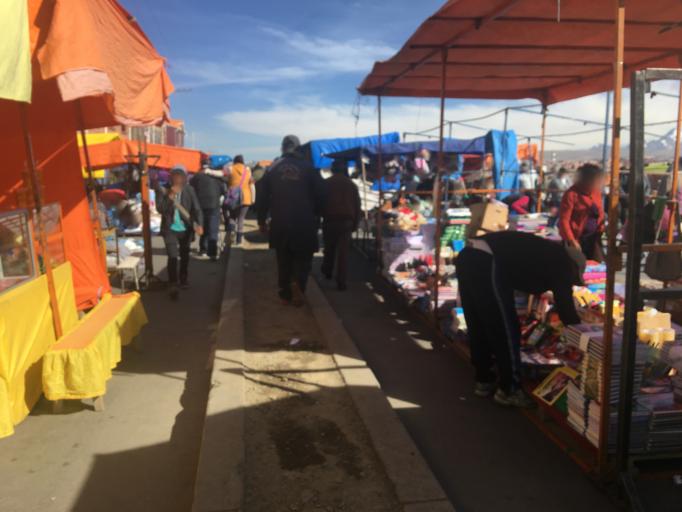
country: BO
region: La Paz
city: La Paz
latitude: -16.4951
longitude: -68.1680
